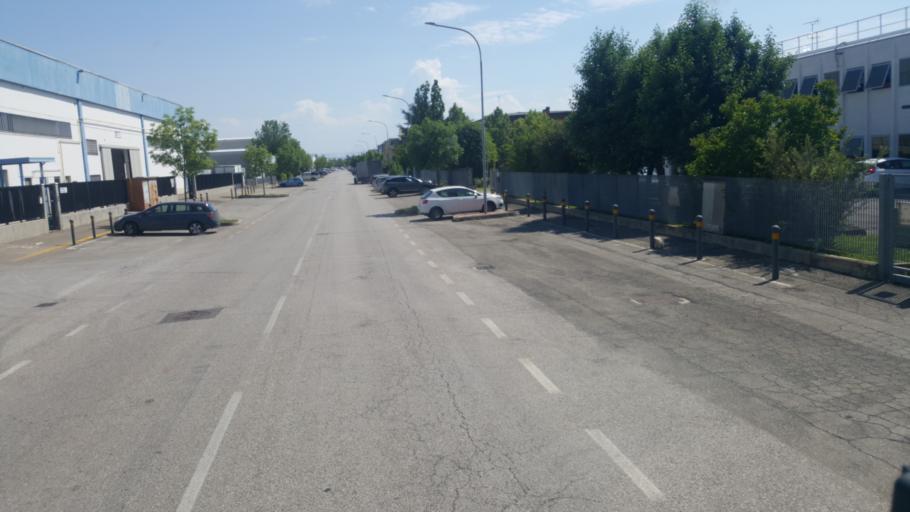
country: IT
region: Emilia-Romagna
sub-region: Provincia di Bologna
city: Castel Maggiore
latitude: 44.6098
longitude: 11.3644
